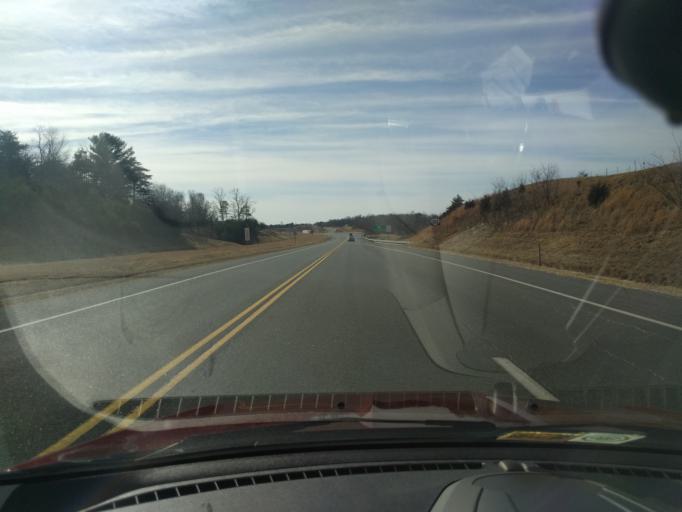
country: US
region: Virginia
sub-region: City of Staunton
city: Staunton
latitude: 38.1579
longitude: -79.1129
